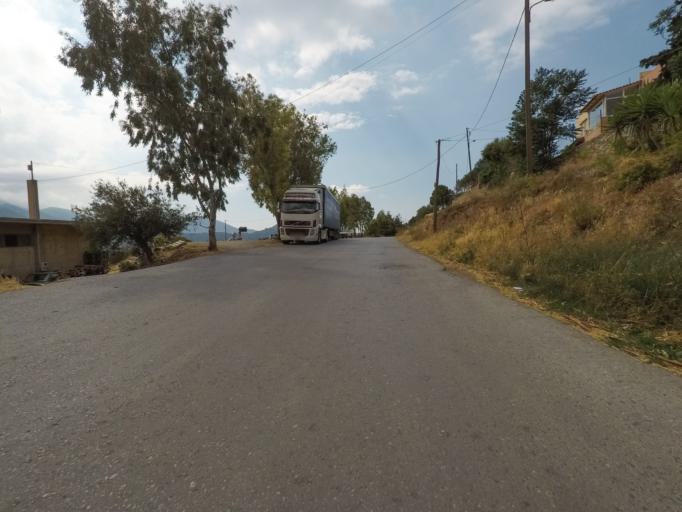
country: GR
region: Crete
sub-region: Nomos Lasithiou
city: Neapoli
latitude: 35.2607
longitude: 25.6110
